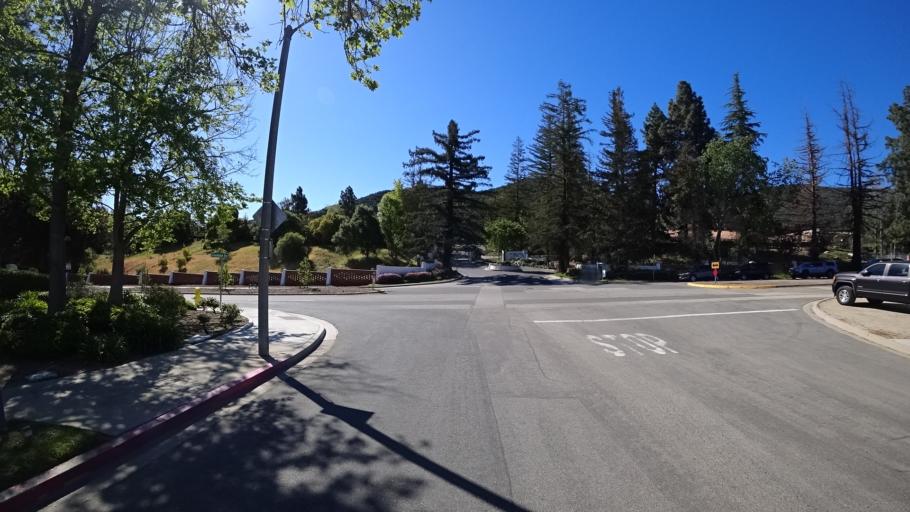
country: US
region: California
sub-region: Ventura County
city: Thousand Oaks
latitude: 34.1721
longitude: -118.8808
